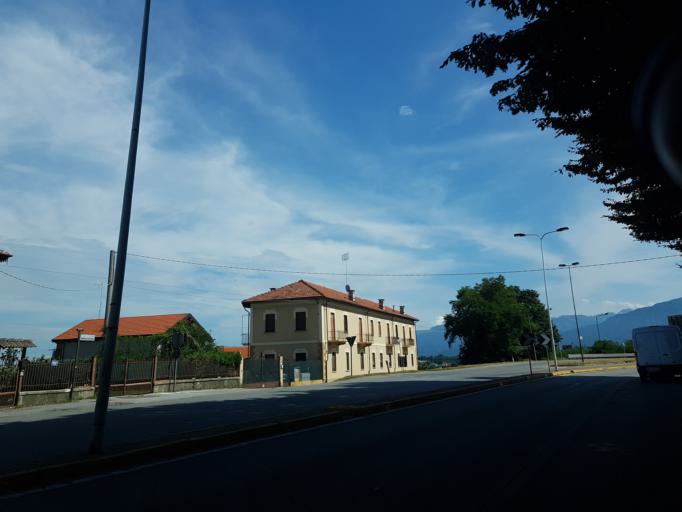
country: IT
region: Piedmont
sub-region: Provincia di Cuneo
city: Cuneo
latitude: 44.4106
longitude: 7.5524
